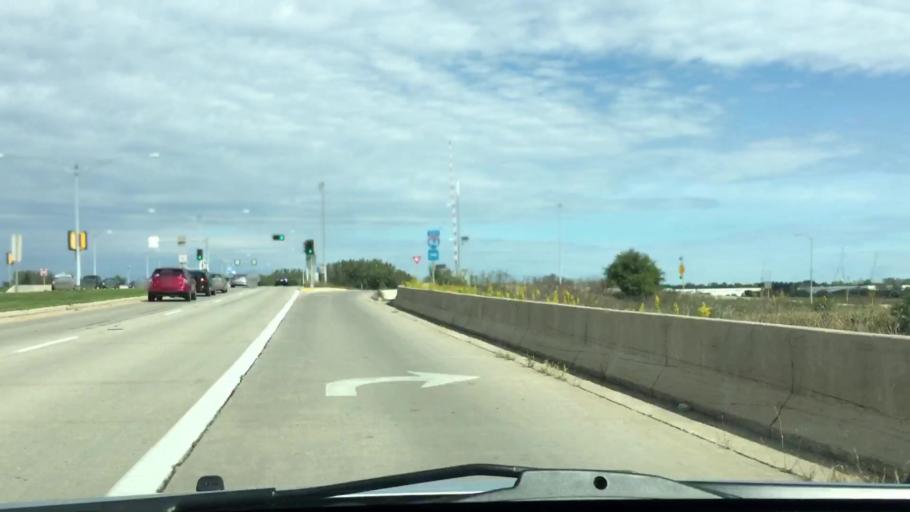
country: US
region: Wisconsin
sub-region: Waukesha County
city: Pewaukee
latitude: 43.0452
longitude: -88.2556
